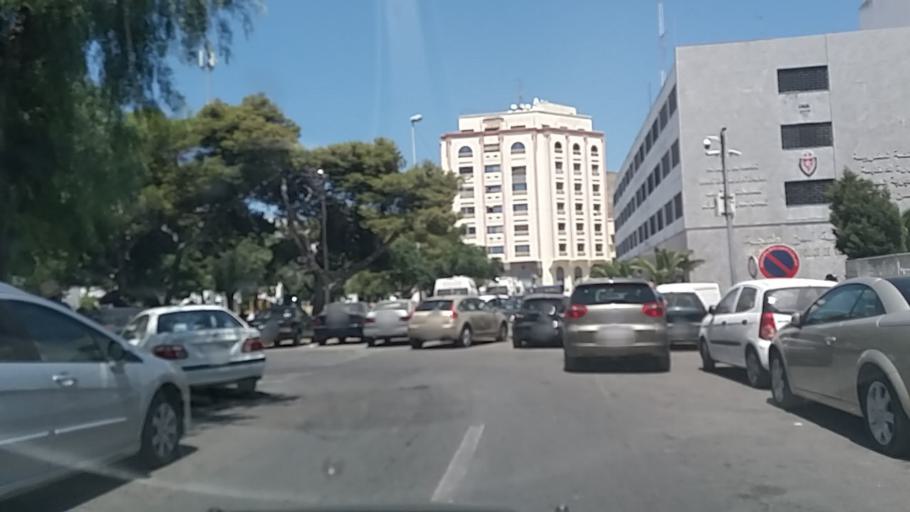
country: MA
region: Tanger-Tetouan
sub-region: Tanger-Assilah
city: Tangier
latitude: 35.7748
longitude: -5.8067
